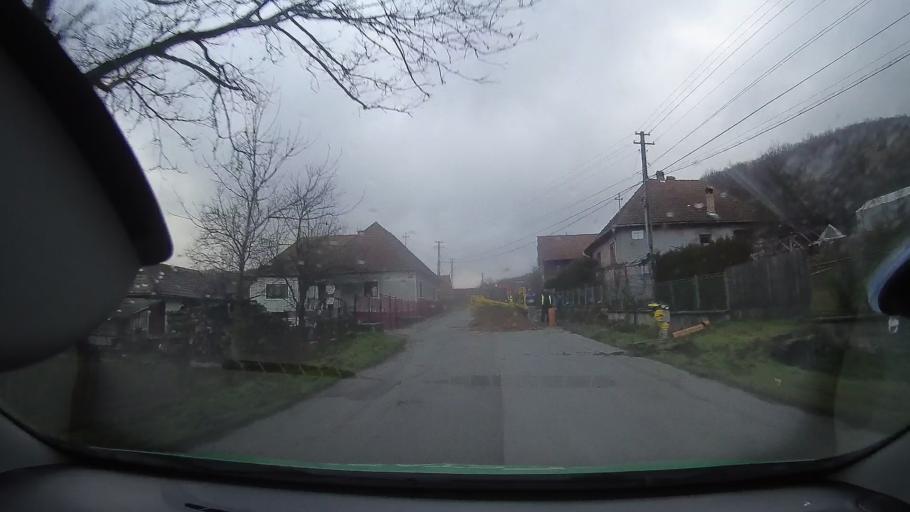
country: RO
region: Hunedoara
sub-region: Comuna Baia de Cris
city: Baia de Cris
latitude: 46.2115
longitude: 22.7153
